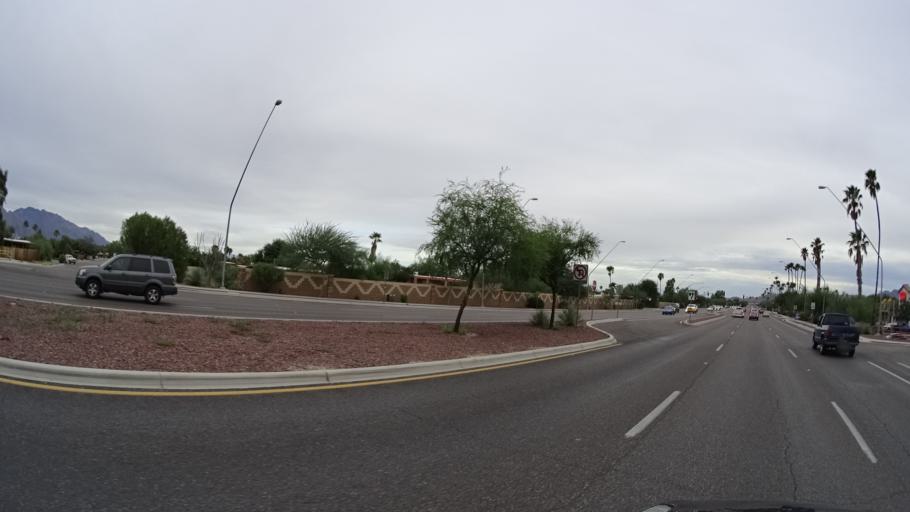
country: US
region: Arizona
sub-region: Pima County
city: Casas Adobes
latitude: 32.3325
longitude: -111.0463
